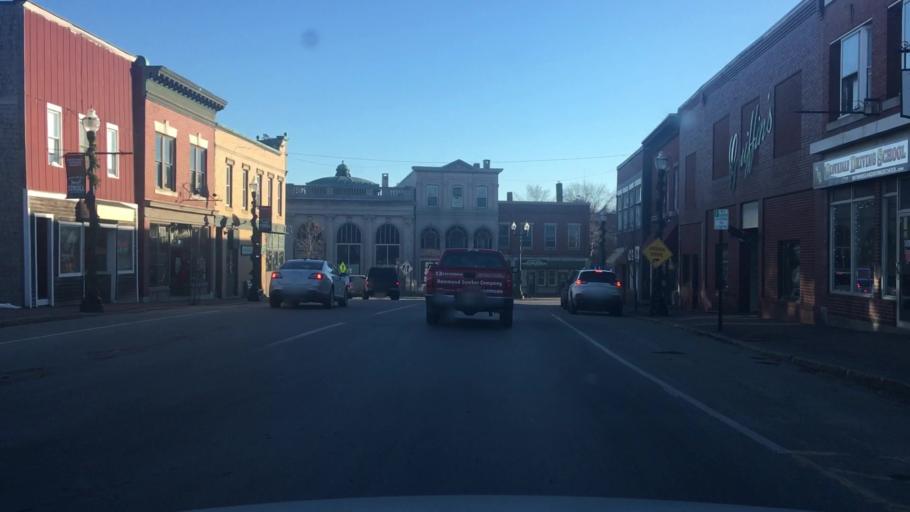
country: US
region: Maine
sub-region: Somerset County
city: Skowhegan
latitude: 44.7657
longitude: -69.7197
